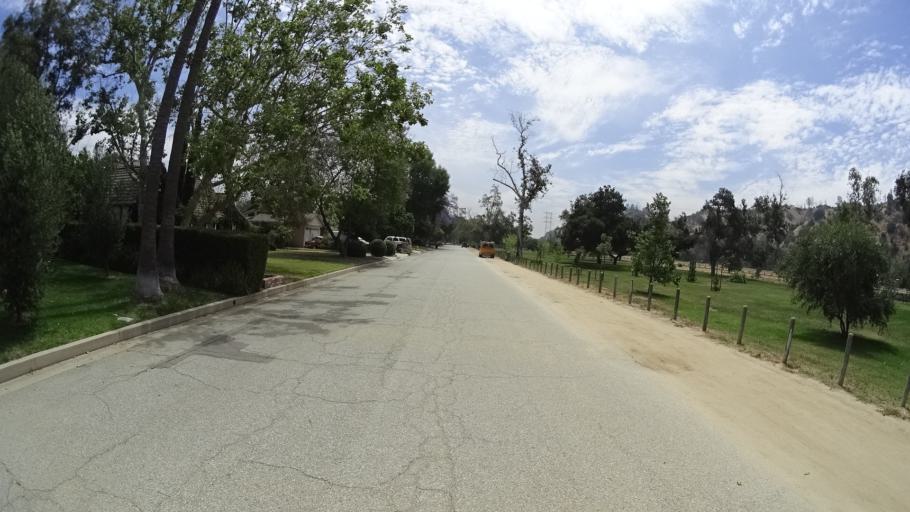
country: US
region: California
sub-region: Los Angeles County
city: Burbank
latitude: 34.1583
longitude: -118.3013
